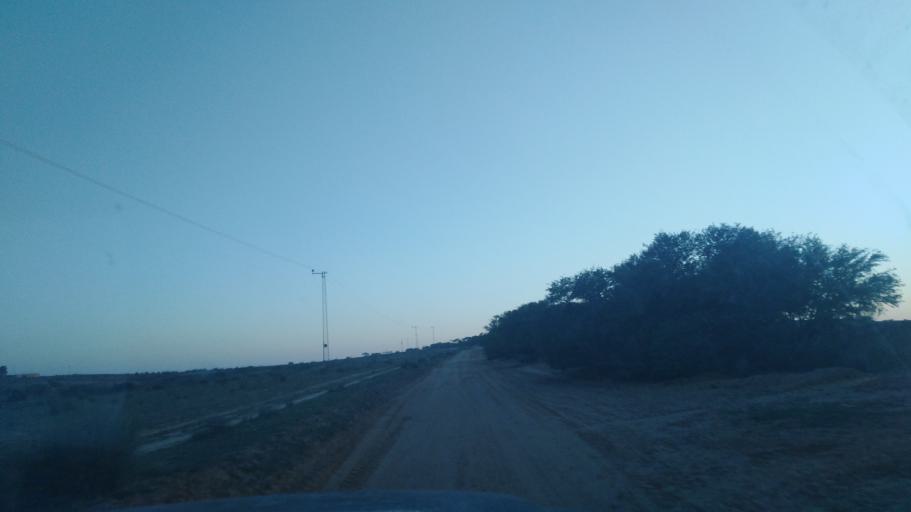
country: TN
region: Safaqis
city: Sfax
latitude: 34.7361
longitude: 10.4450
